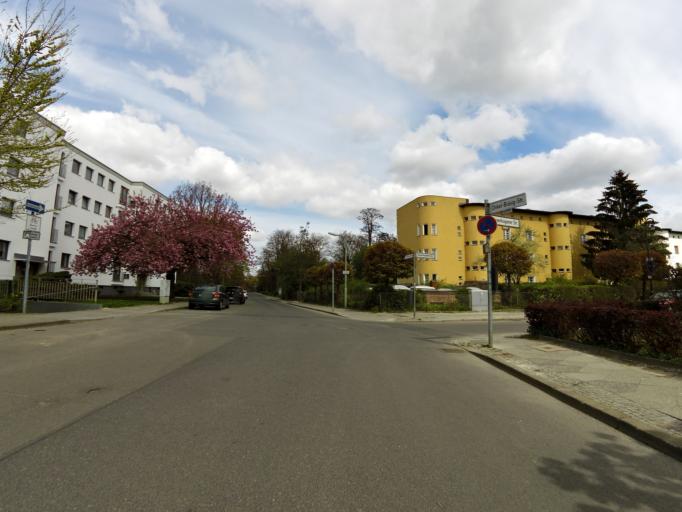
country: DE
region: Berlin
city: Britz
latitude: 52.4509
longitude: 13.4455
